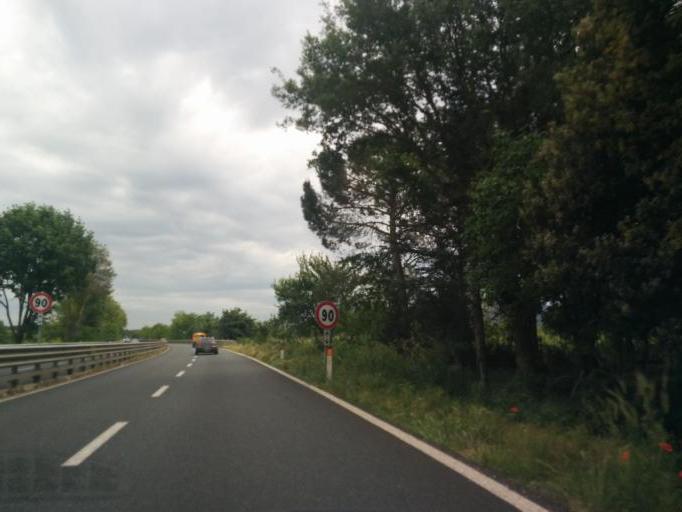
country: IT
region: Tuscany
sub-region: Provincia di Siena
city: Staggia
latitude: 43.4111
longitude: 11.1656
